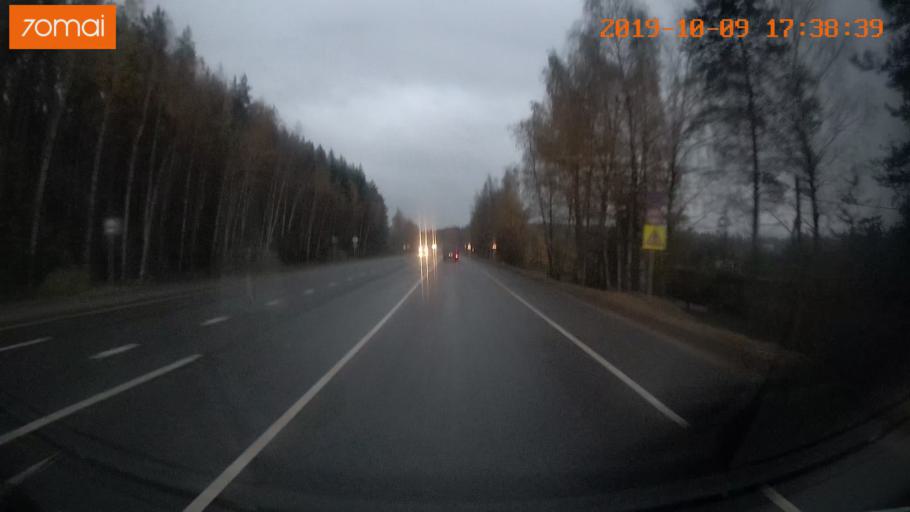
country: RU
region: Ivanovo
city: Bogorodskoye
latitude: 57.0689
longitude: 40.9516
